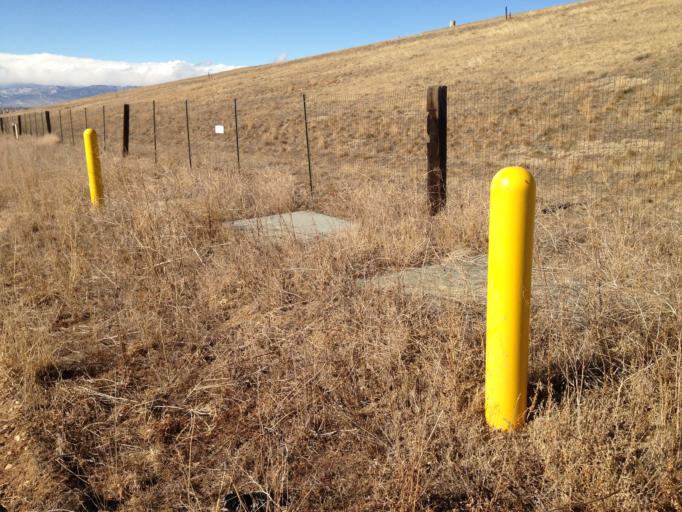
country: US
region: Colorado
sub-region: Boulder County
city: Erie
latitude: 40.0294
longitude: -105.0315
